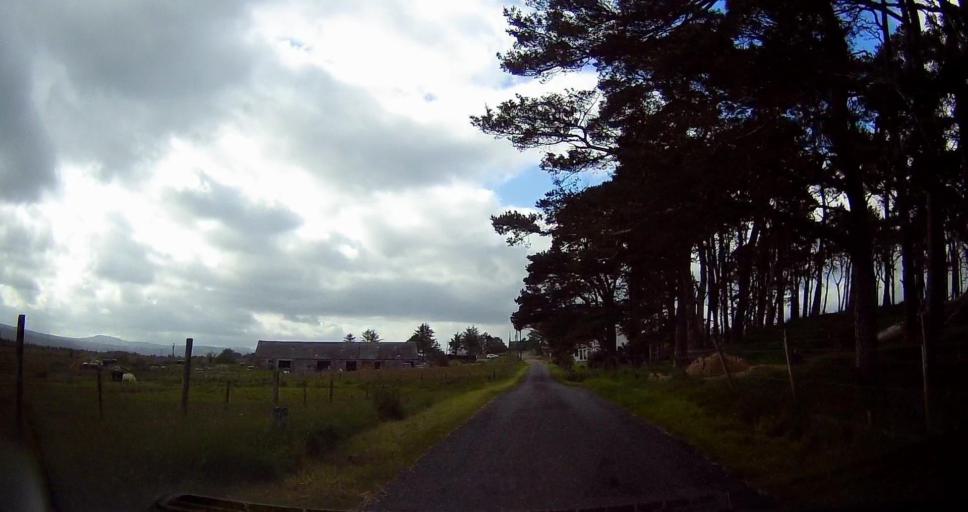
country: GB
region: Scotland
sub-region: Highland
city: Alness
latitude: 58.0708
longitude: -4.4320
